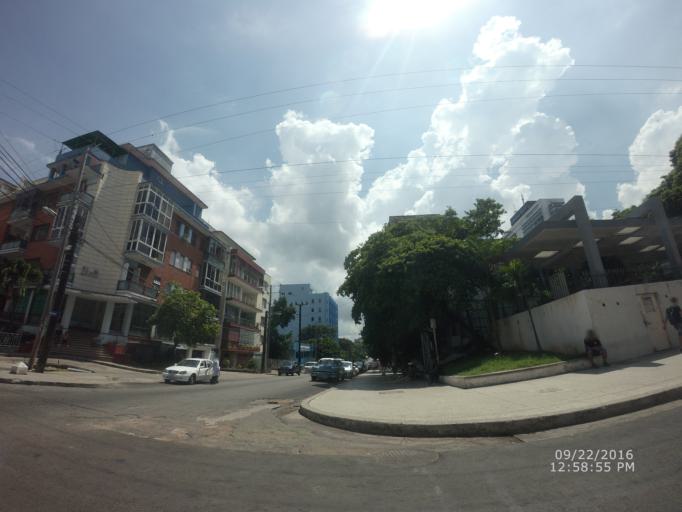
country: CU
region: La Habana
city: Havana
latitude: 23.1420
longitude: -82.3827
